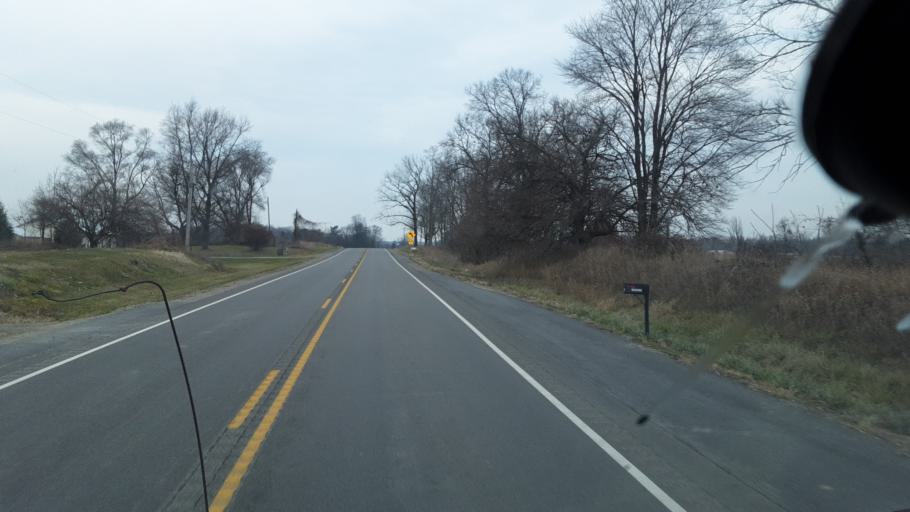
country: US
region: Indiana
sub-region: Steuben County
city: Angola
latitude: 41.6219
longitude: -85.1699
